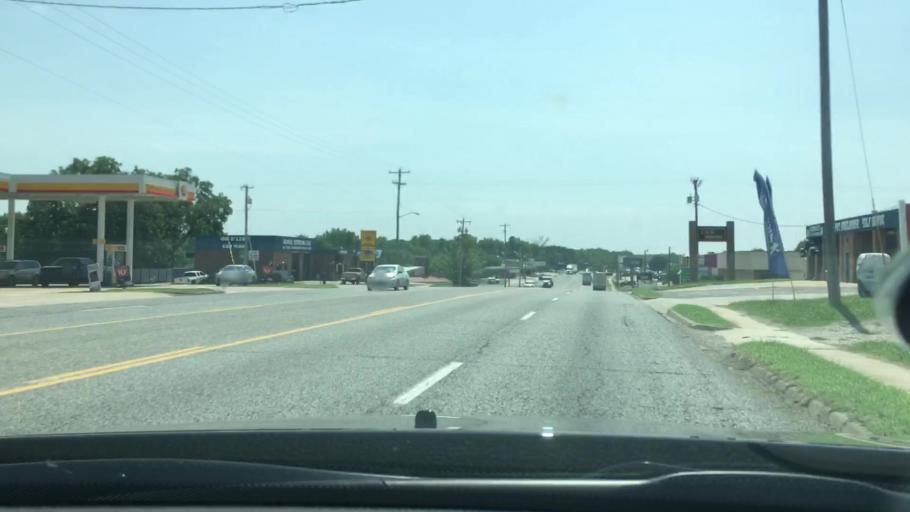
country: US
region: Oklahoma
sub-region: Atoka County
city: Atoka
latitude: 34.3837
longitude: -96.1293
